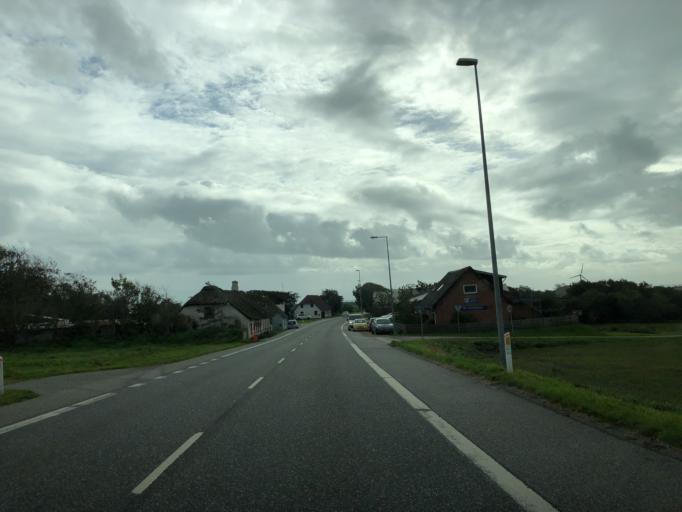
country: DK
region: North Denmark
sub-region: Thisted Kommune
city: Hurup
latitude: 56.7071
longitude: 8.4127
